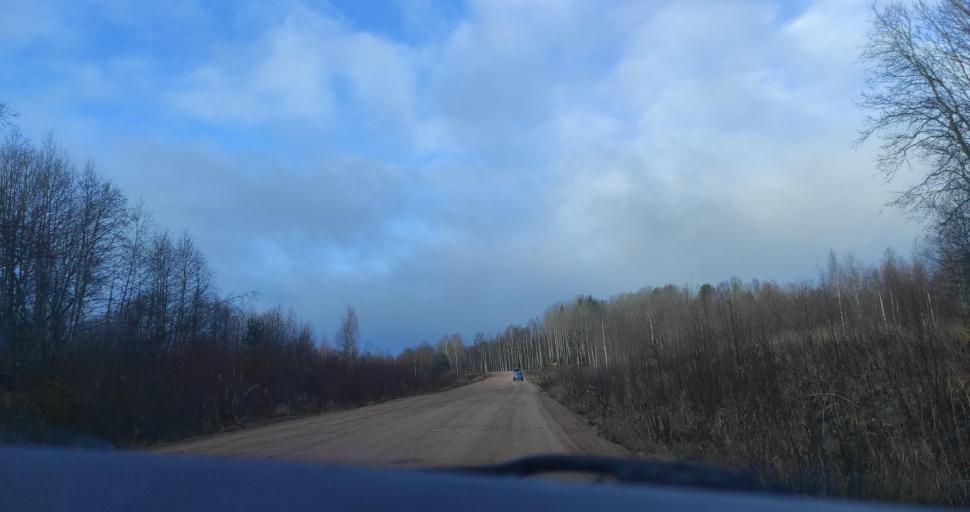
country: RU
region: Republic of Karelia
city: Pitkyaranta
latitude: 61.7124
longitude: 31.3566
